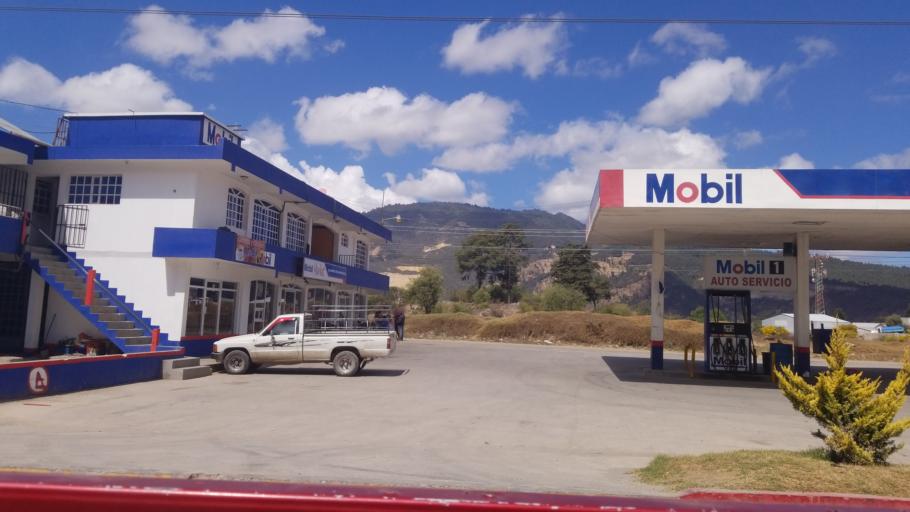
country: GT
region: Quetzaltenango
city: Quetzaltenango
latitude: 14.8191
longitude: -91.5365
